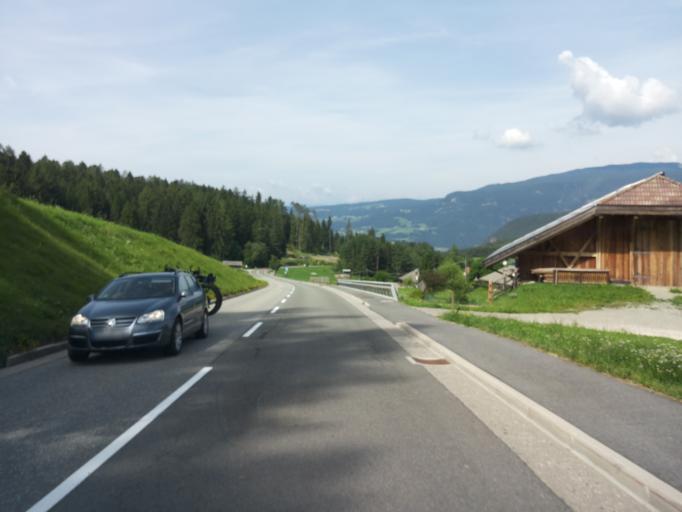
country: IT
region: Trentino-Alto Adige
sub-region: Bolzano
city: Castelrotto
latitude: 46.5716
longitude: 11.5878
